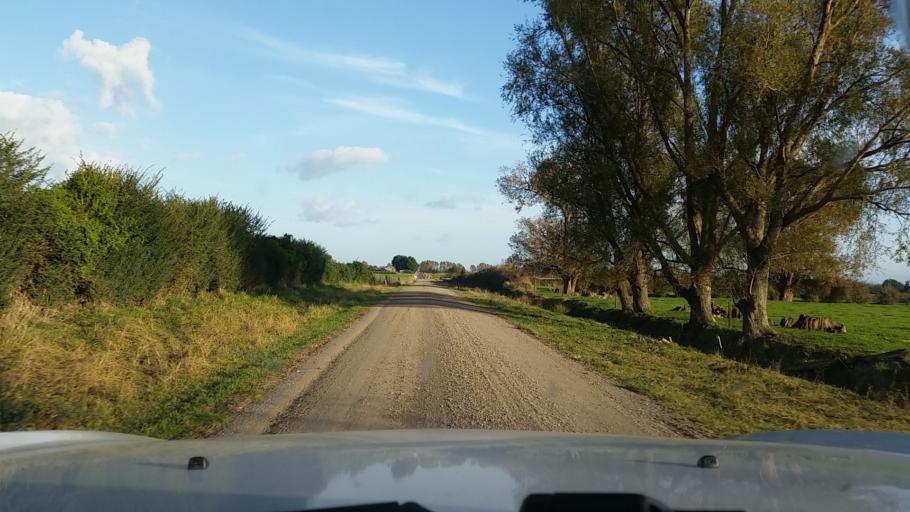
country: NZ
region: Bay of Plenty
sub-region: Western Bay of Plenty District
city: Katikati
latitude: -37.5902
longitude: 175.7132
